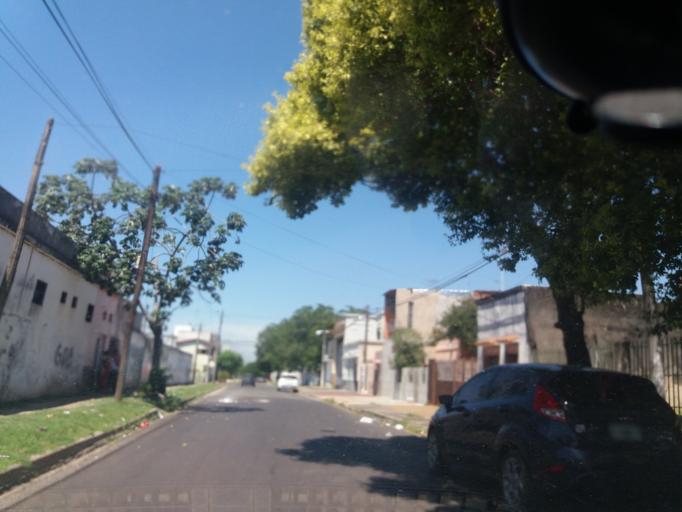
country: AR
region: Corrientes
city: Corrientes
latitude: -27.4825
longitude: -58.8454
